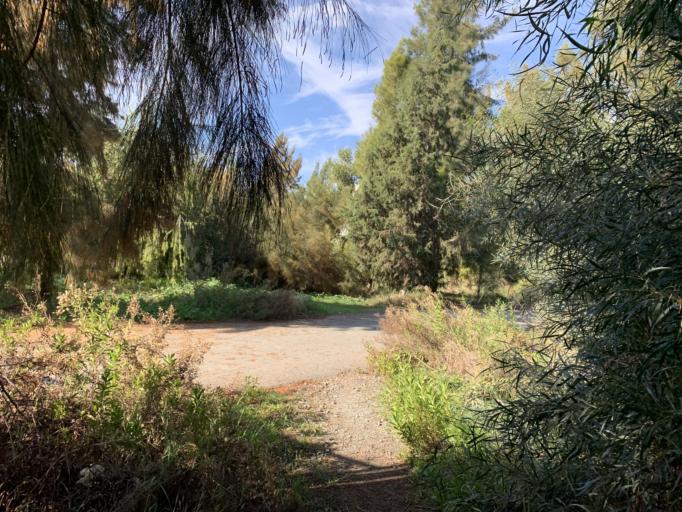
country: CY
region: Larnaka
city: Larnaca
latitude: 34.9107
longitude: 33.6108
